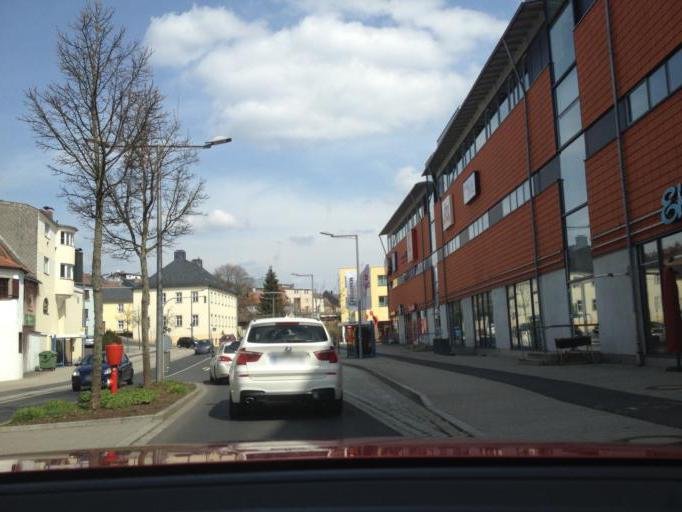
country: DE
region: Bavaria
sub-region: Upper Franconia
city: Marktredwitz
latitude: 50.0005
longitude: 12.0872
